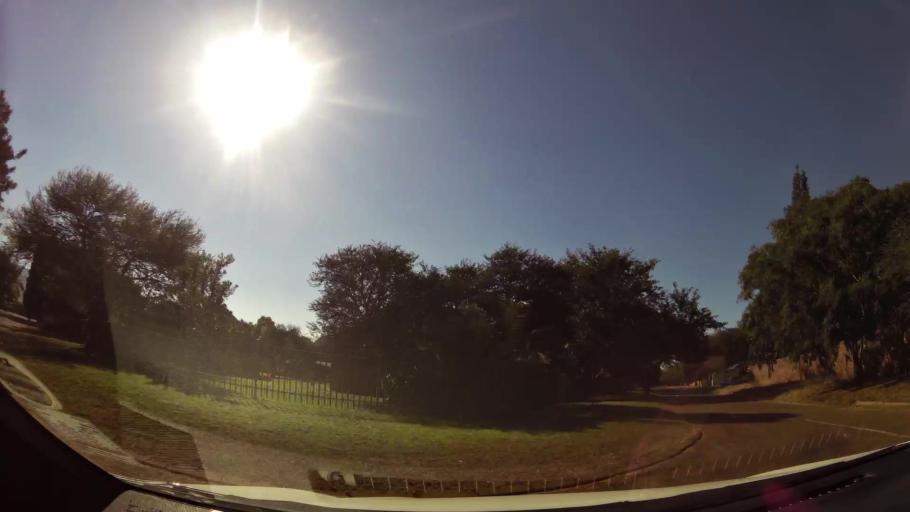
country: ZA
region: Limpopo
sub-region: Waterberg District Municipality
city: Mokopane
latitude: -24.2107
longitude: 28.9948
